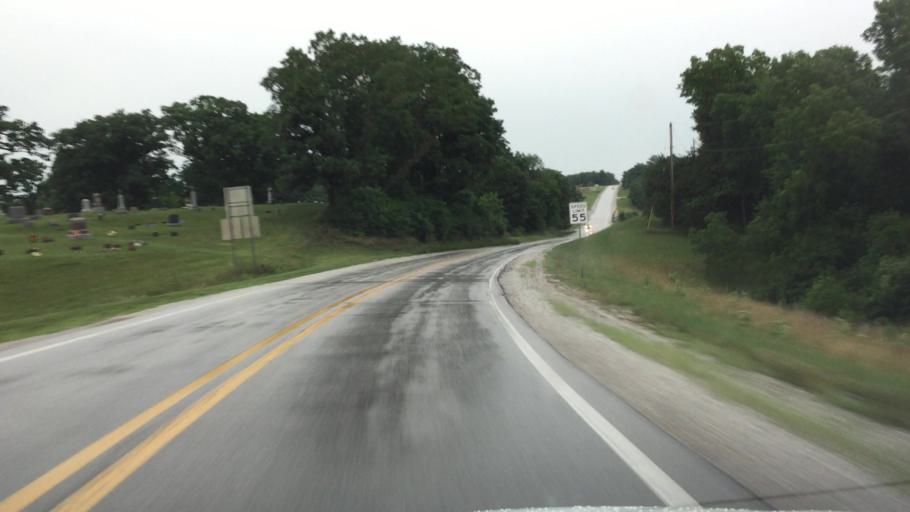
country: US
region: Illinois
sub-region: Hancock County
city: Carthage
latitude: 40.4271
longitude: -91.1401
